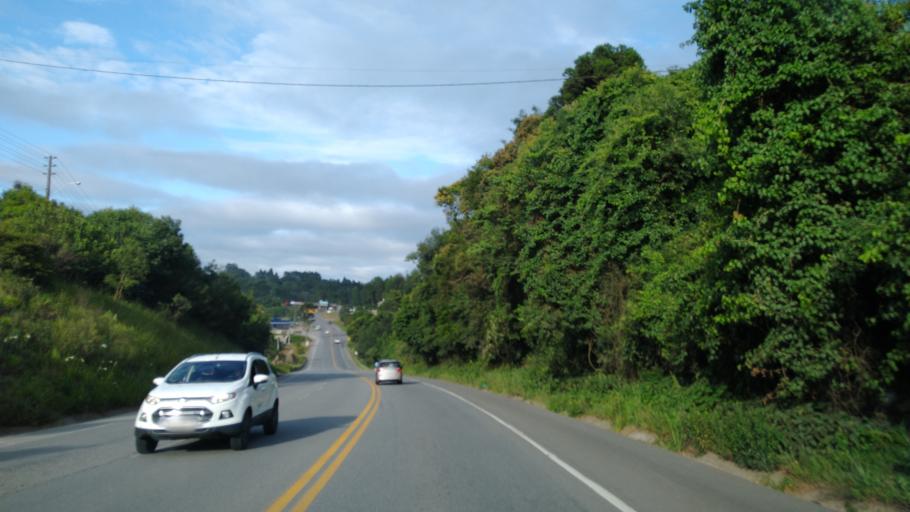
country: BR
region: Santa Catarina
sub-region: Sao Bento Do Sul
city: Sao Bento do Sul
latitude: -26.2382
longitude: -49.4328
